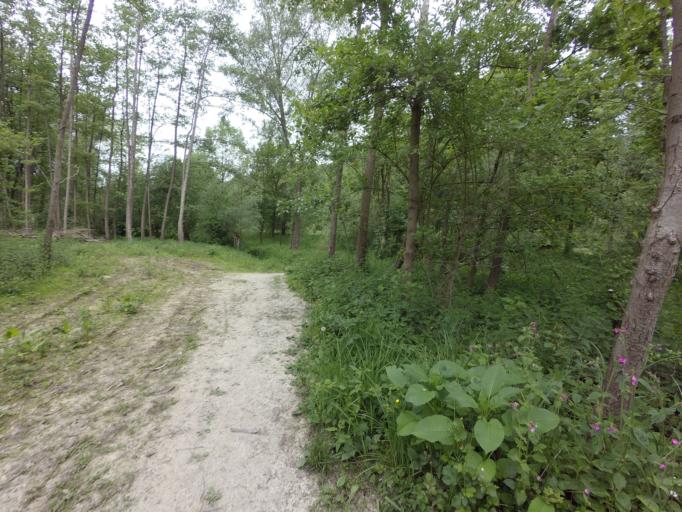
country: NL
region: Limburg
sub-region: Gemeente Voerendaal
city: Ubachsberg
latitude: 50.8256
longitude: 5.9204
